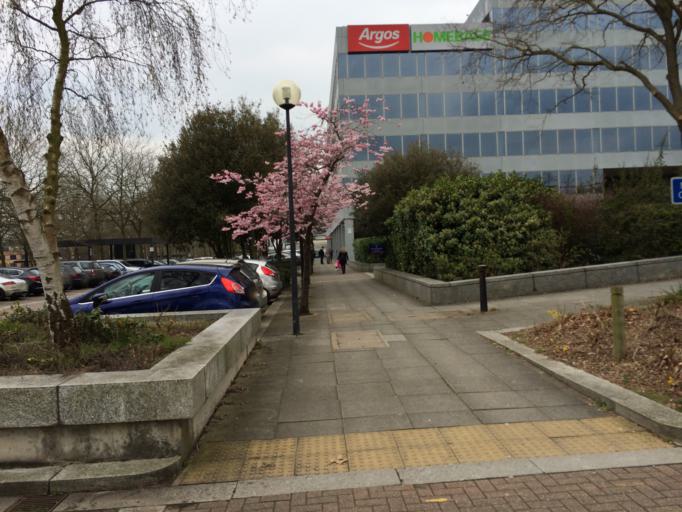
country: GB
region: England
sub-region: Milton Keynes
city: Milton Keynes
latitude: 52.0391
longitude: -0.7583
